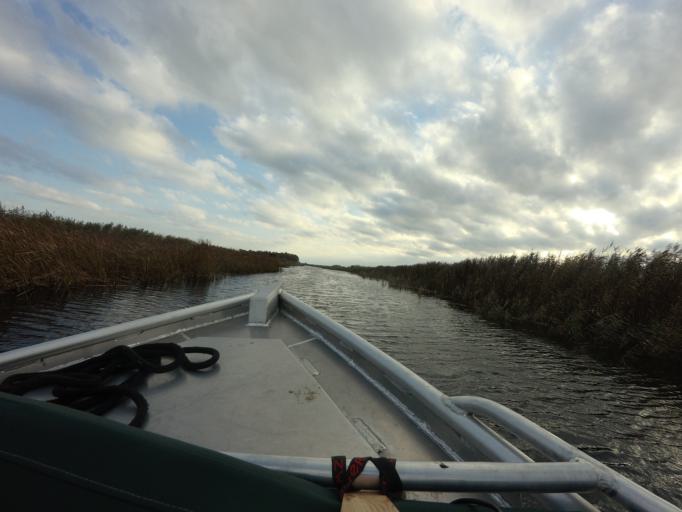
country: NL
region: Overijssel
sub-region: Gemeente Steenwijkerland
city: Blokzijl
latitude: 52.7381
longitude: 5.9754
